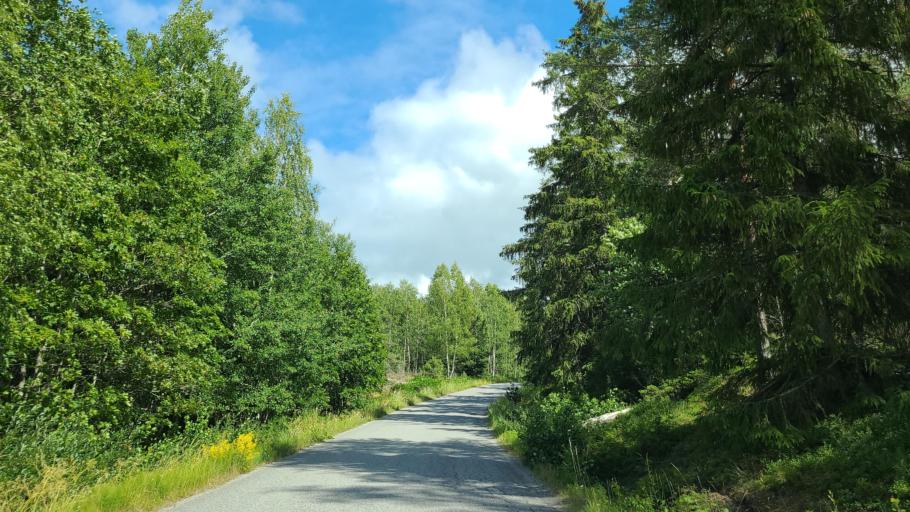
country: FI
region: Varsinais-Suomi
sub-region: Aboland-Turunmaa
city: Nagu
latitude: 60.1752
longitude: 22.0323
